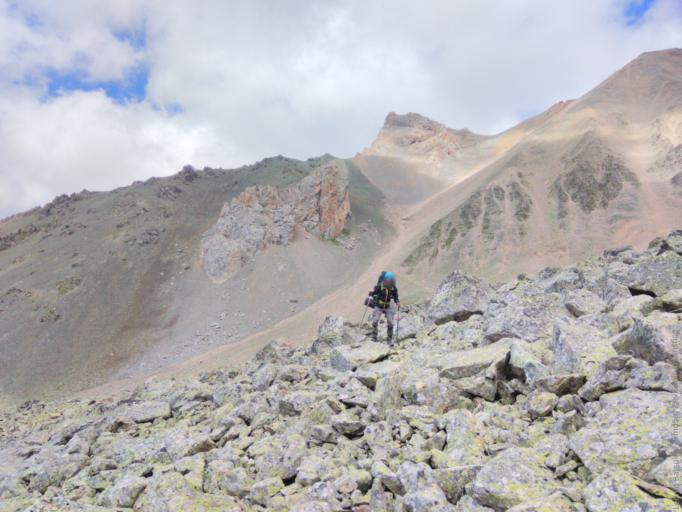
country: RU
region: Kabardino-Balkariya
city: Tyrnyauz
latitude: 43.3860
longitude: 42.7957
